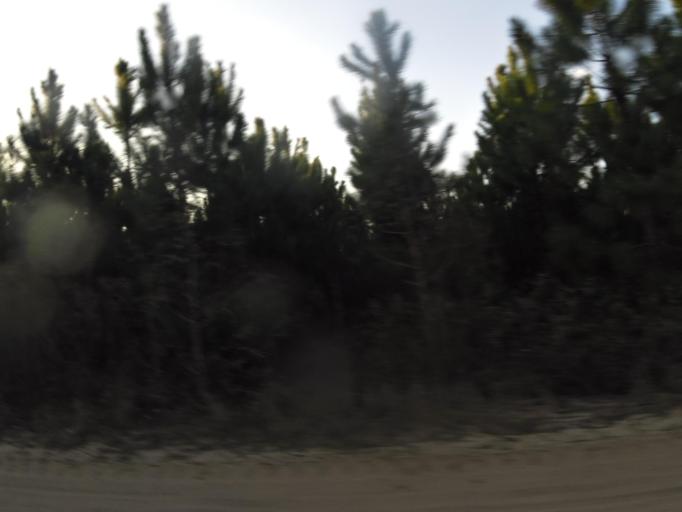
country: US
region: Florida
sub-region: Clay County
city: Keystone Heights
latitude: 29.8181
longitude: -81.8352
